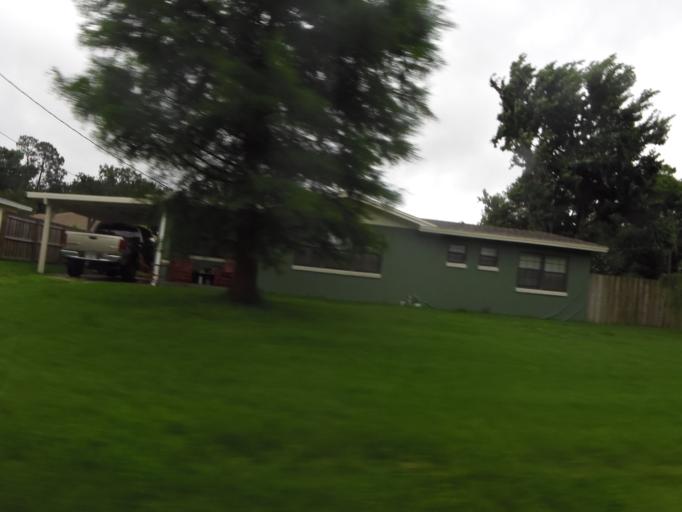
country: US
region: Florida
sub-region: Duval County
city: Jacksonville
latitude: 30.2810
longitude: -81.6259
